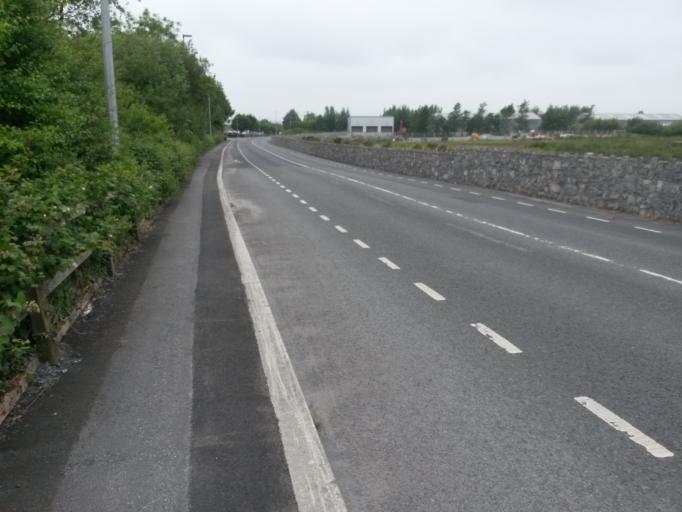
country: IE
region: Munster
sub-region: An Clar
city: Ennis
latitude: 52.8388
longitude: -8.9683
